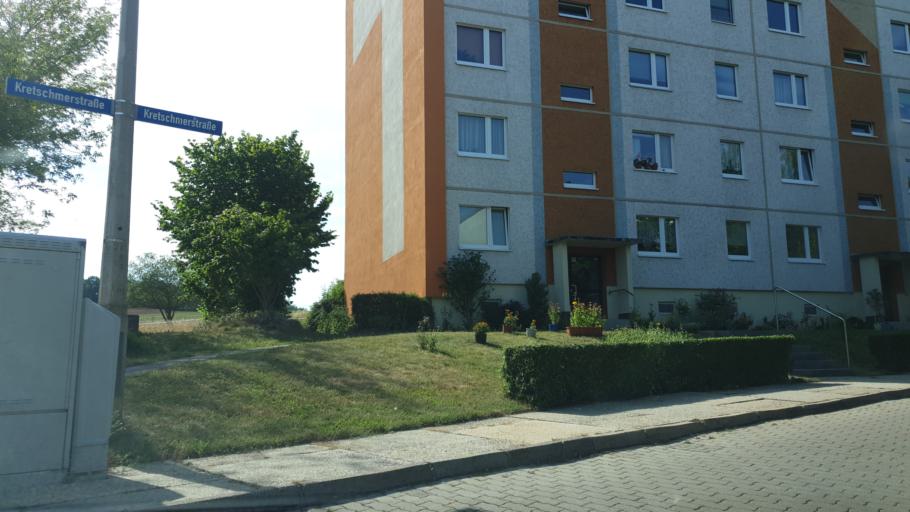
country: DE
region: Thuringia
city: Zedlitz
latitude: 50.8389
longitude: 12.0463
